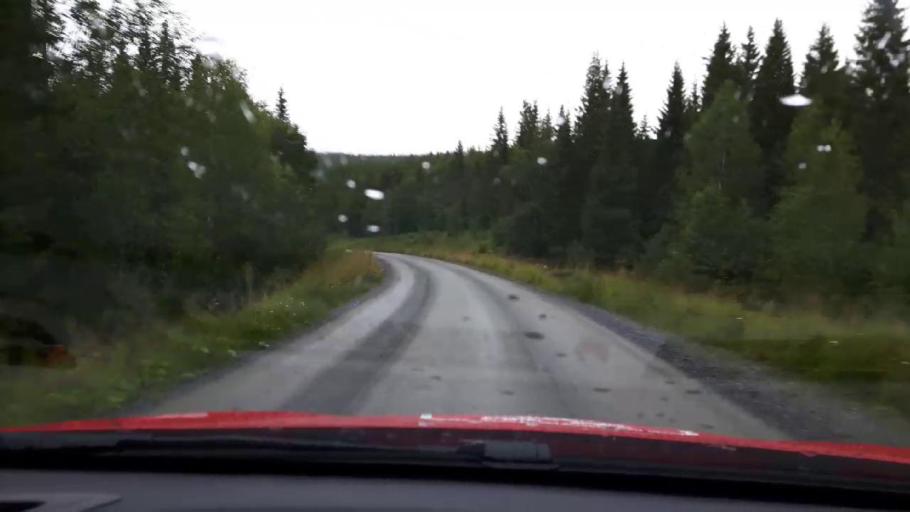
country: SE
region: Jaemtland
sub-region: Are Kommun
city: Are
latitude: 63.4759
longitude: 12.8093
